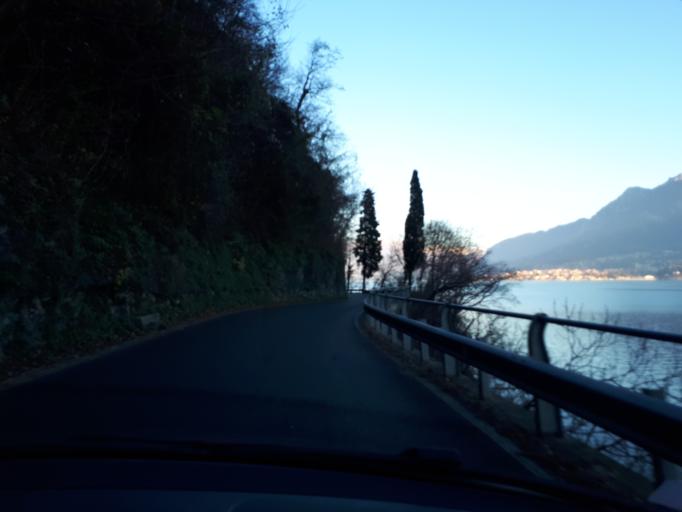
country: IT
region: Lombardy
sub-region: Provincia di Lecco
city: Abbadia Lariana
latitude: 45.8885
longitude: 9.3198
